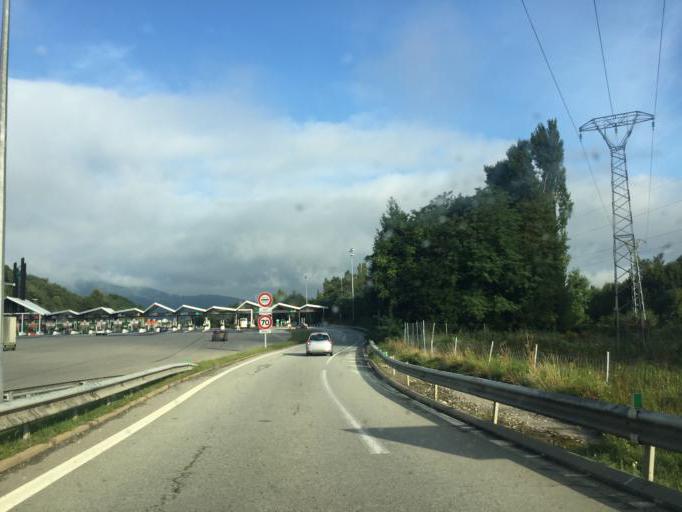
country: FR
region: Rhone-Alpes
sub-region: Departement de la Savoie
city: Les Marches
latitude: 45.5122
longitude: 6.0051
